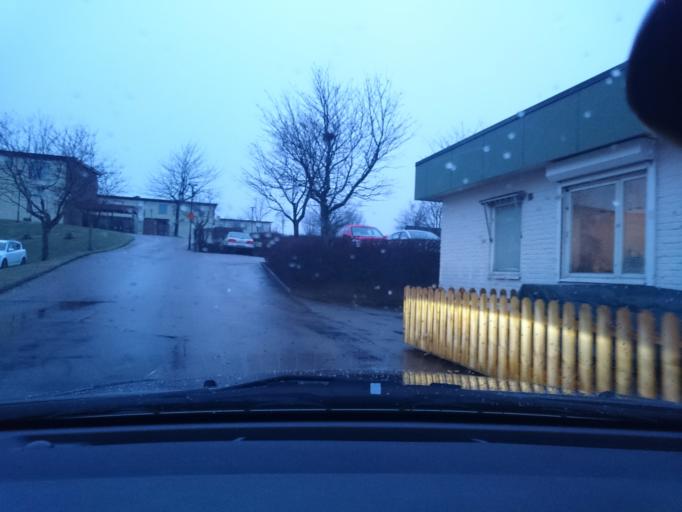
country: SE
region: Skane
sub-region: Bastads Kommun
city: Forslov
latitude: 56.3478
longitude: 12.8162
